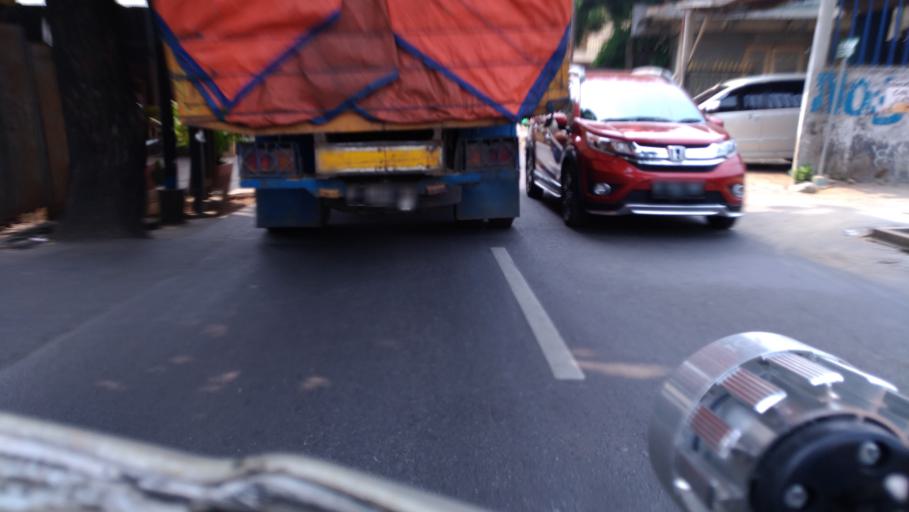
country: ID
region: West Java
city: Depok
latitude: -6.3393
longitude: 106.8812
